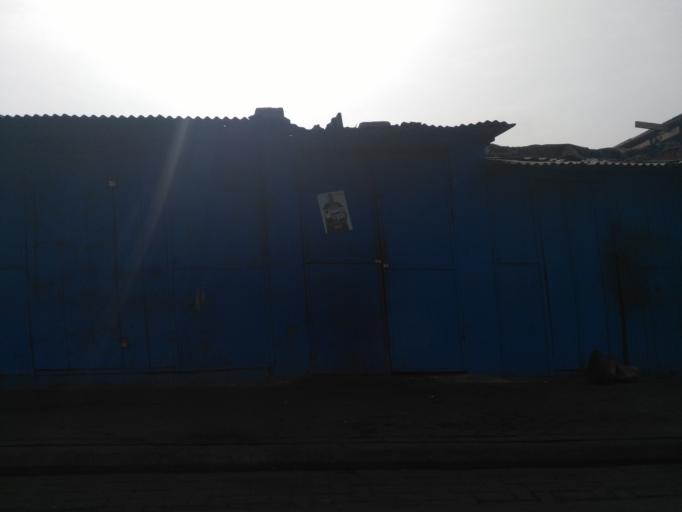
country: GH
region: Greater Accra
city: Accra
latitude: 5.5381
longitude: -0.2091
